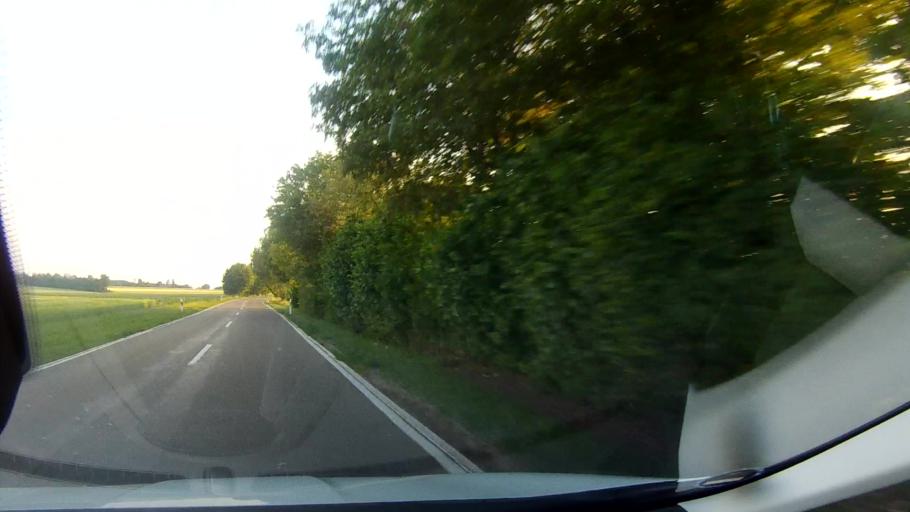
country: DE
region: Baden-Wuerttemberg
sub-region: Tuebingen Region
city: Huttisheim
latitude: 48.2836
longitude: 9.9615
